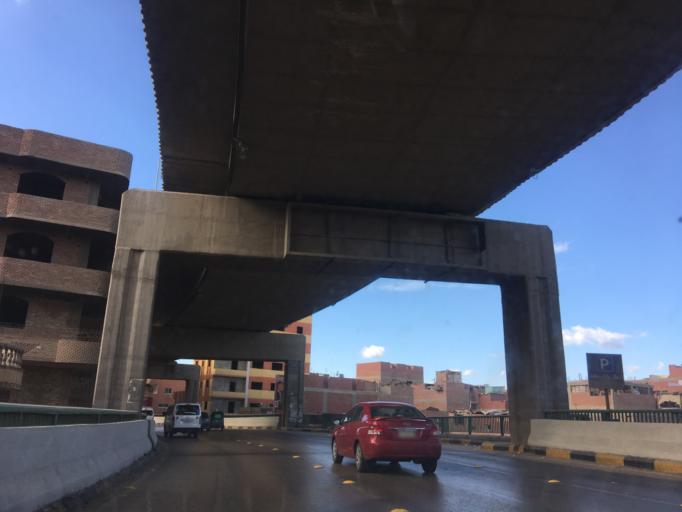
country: EG
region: Al Jizah
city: Al Jizah
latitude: 30.0309
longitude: 31.1723
